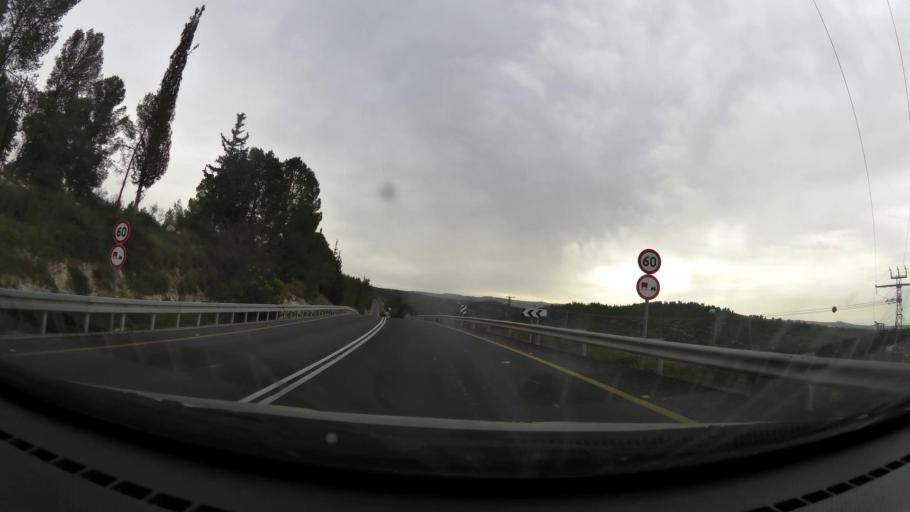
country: PS
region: West Bank
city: Surif
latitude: 31.6732
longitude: 35.0209
